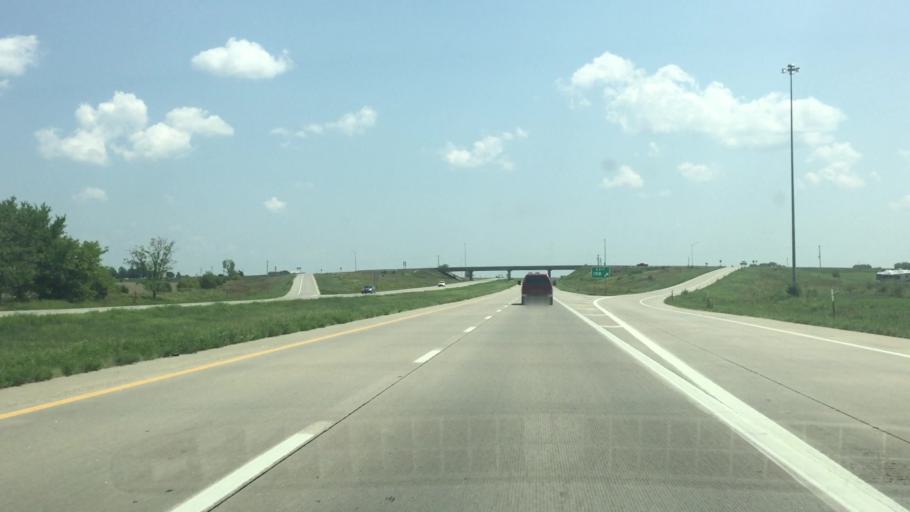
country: US
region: Kansas
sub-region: Franklin County
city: Wellsville
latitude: 38.7028
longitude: -95.0803
